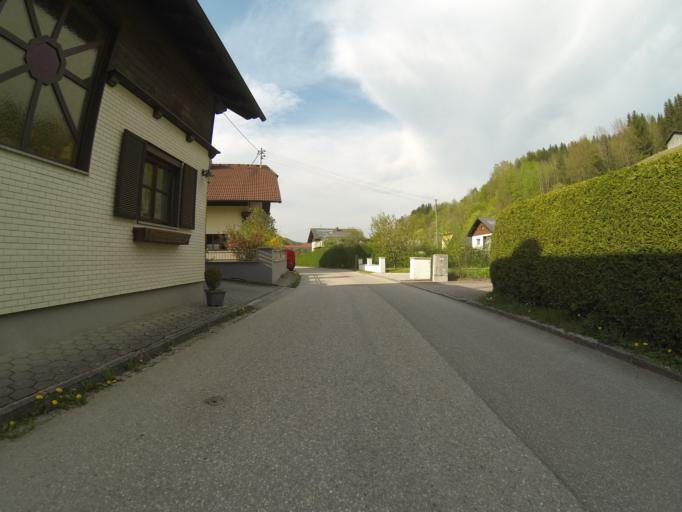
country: AT
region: Upper Austria
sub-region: Politischer Bezirk Gmunden
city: Altmunster
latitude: 47.9264
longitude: 13.7536
